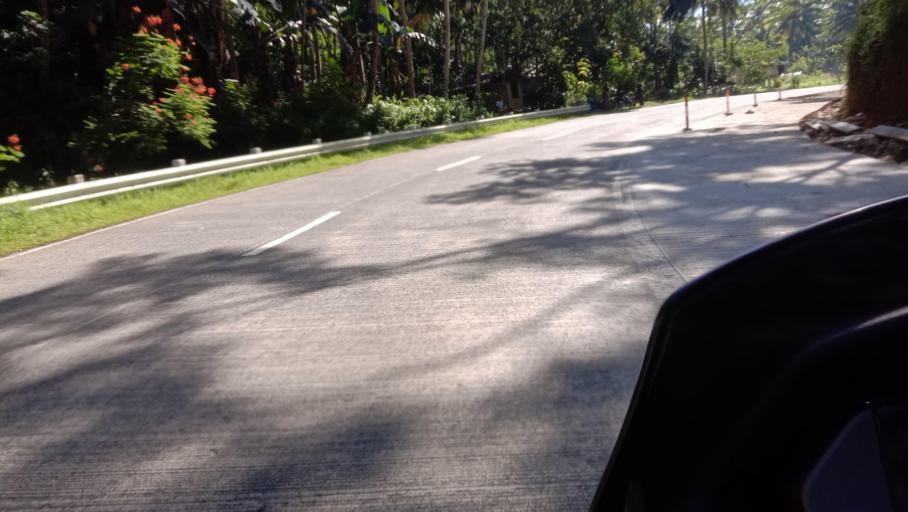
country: PH
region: Caraga
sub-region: Province of Surigao del Sur
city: Amaga
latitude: 8.5366
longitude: 126.0874
